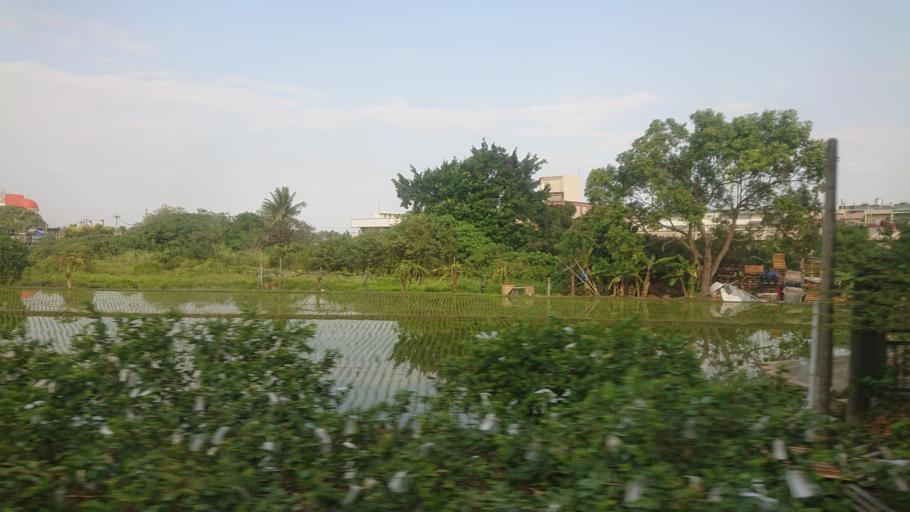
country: TW
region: Taiwan
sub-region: Yunlin
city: Douliu
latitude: 23.7025
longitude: 120.5291
